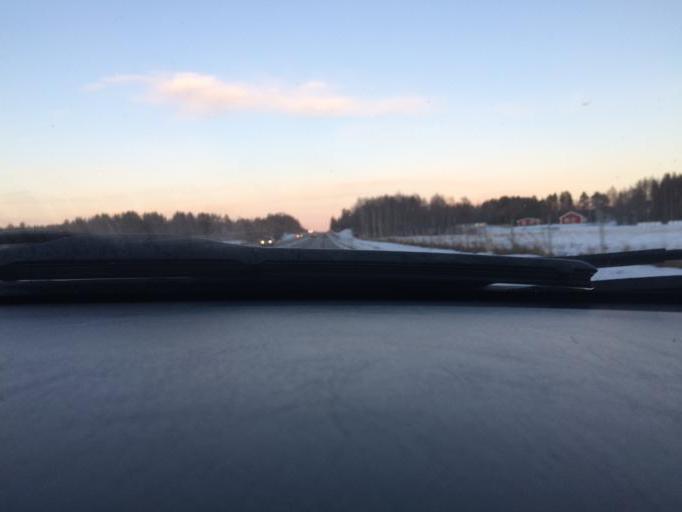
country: SE
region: Norrbotten
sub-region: Lulea Kommun
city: Bergnaset
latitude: 65.6758
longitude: 22.1035
